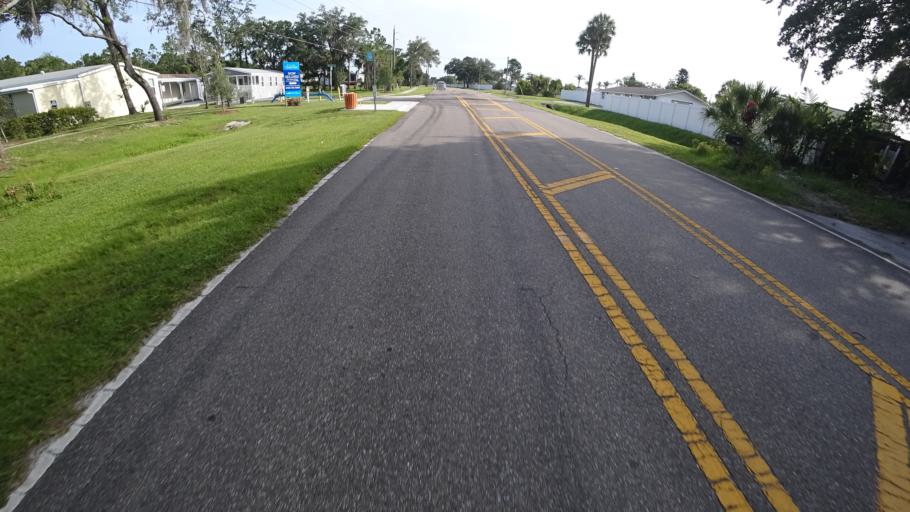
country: US
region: Florida
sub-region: Manatee County
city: Ellenton
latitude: 27.5425
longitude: -82.4912
